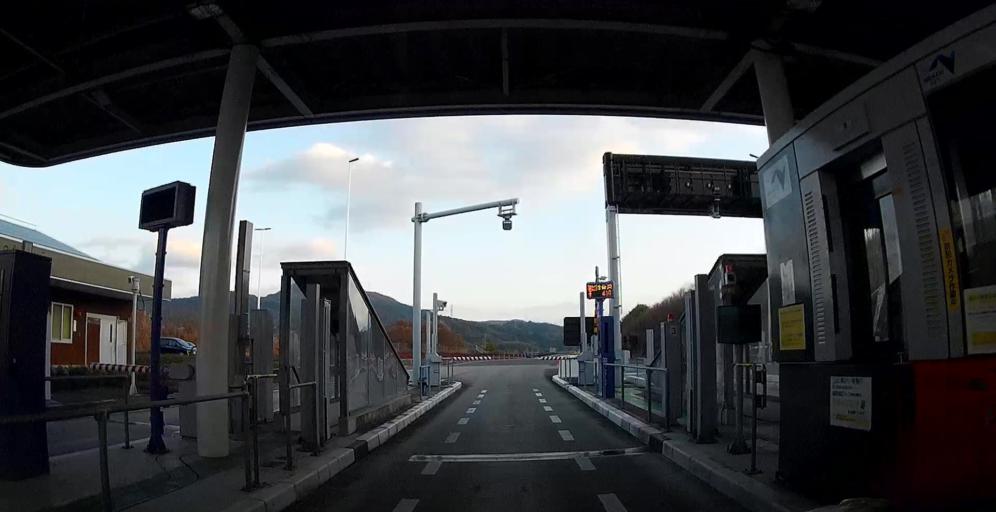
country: JP
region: Kumamoto
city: Kumamoto
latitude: 32.7514
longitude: 130.7974
